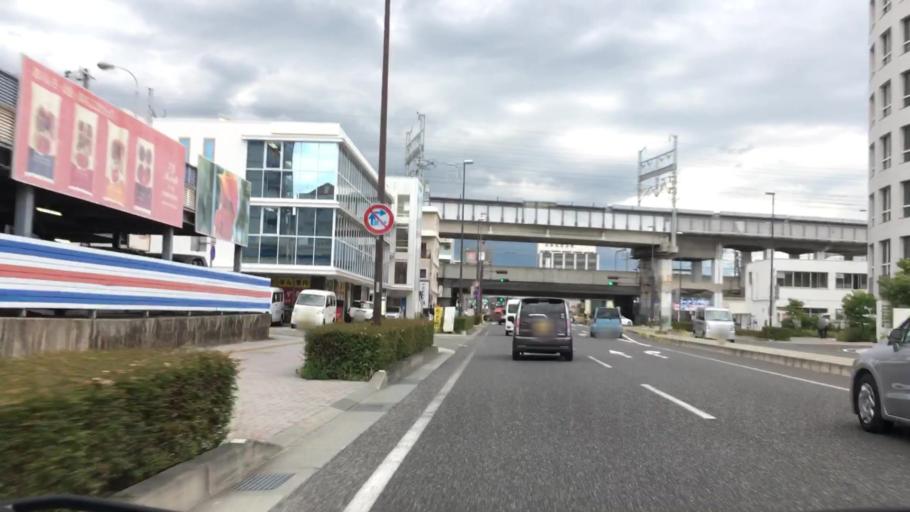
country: JP
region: Hyogo
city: Himeji
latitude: 34.8249
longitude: 134.6947
